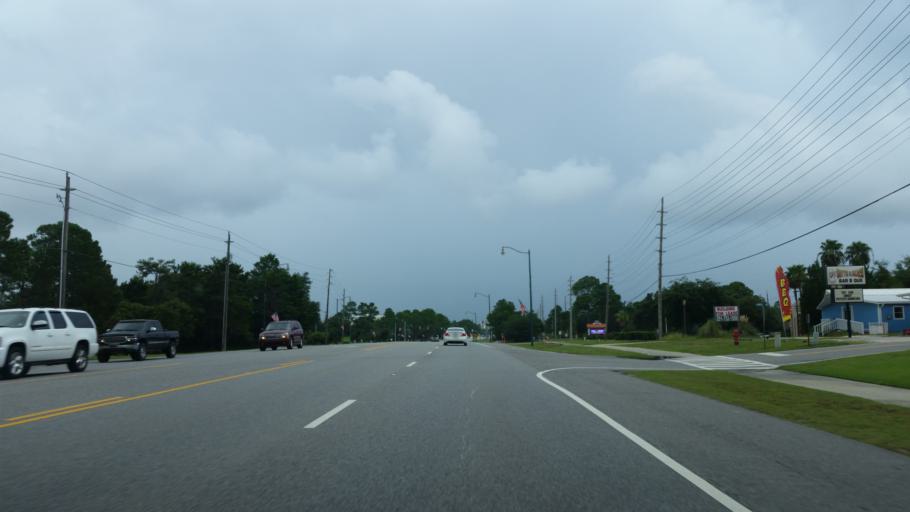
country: US
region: Alabama
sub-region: Baldwin County
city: Orange Beach
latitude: 30.2862
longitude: -87.5813
